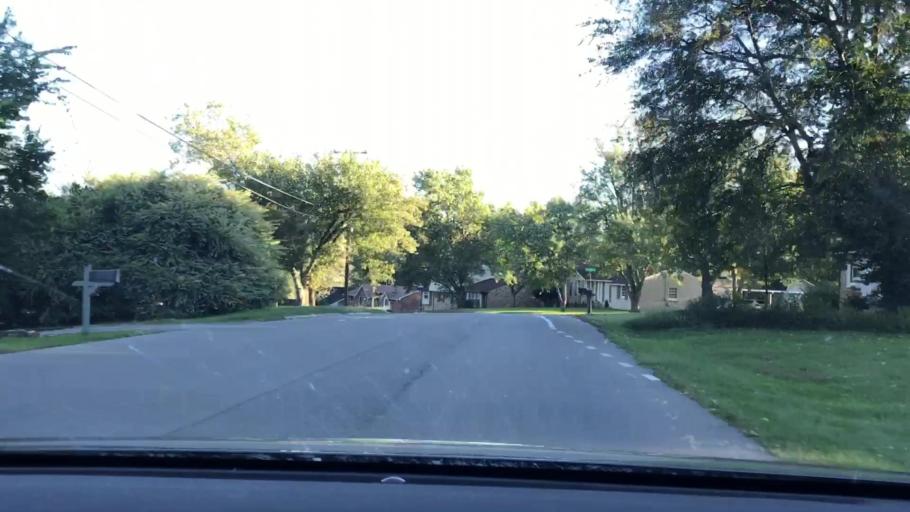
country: US
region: Tennessee
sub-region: Williamson County
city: Brentwood Estates
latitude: 36.0547
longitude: -86.7038
